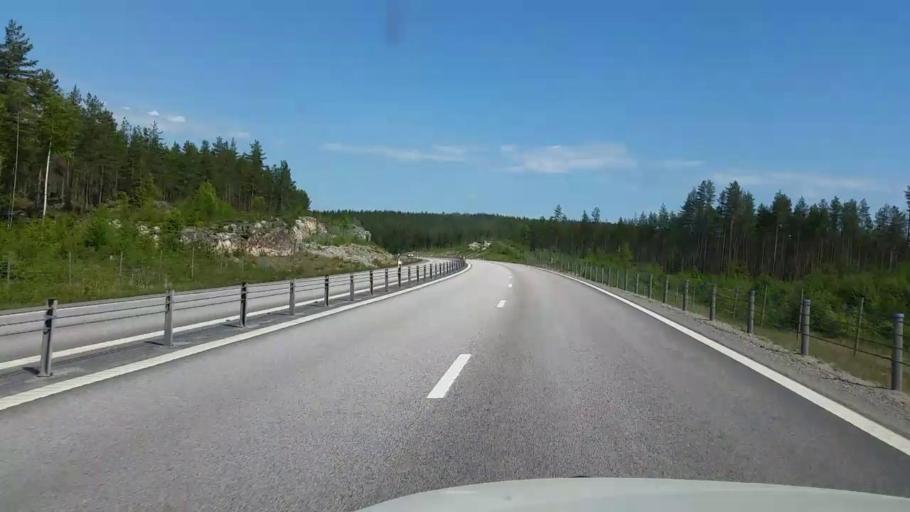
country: SE
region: Gaevleborg
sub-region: Hudiksvalls Kommun
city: Hudiksvall
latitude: 61.7221
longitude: 17.0607
